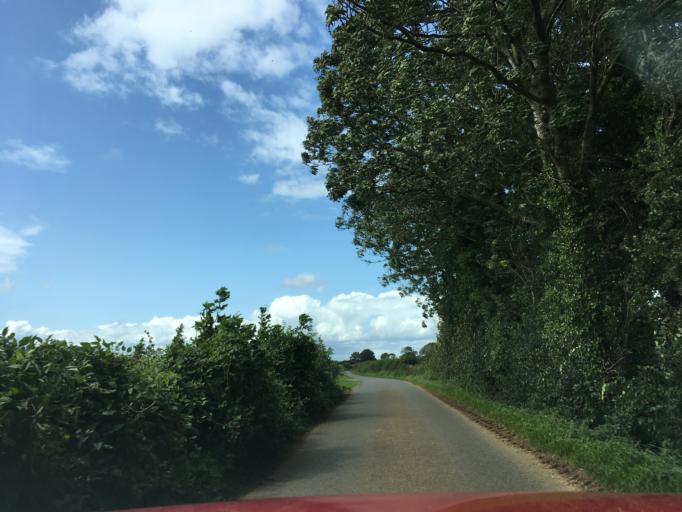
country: GB
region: England
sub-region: Wiltshire
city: Luckington
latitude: 51.5955
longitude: -2.2371
